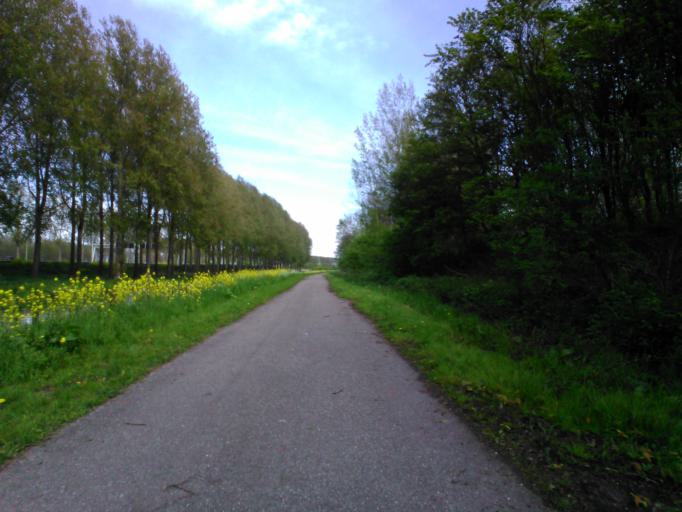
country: NL
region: South Holland
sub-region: Bodegraven-Reeuwijk
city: Bodegraven
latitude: 52.0646
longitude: 4.7417
